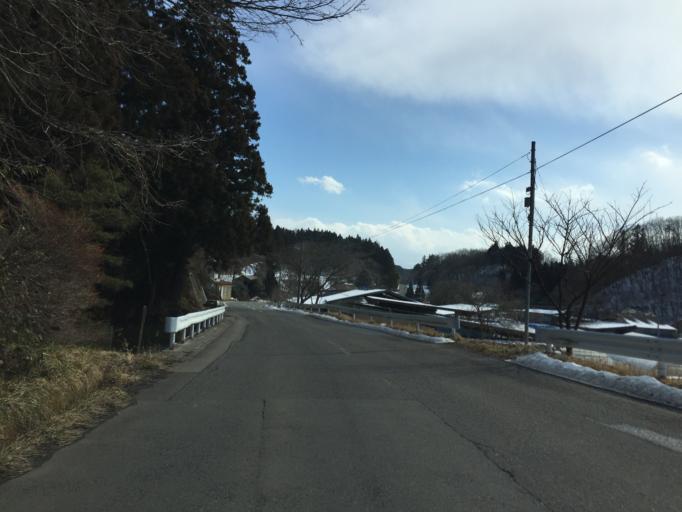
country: JP
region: Fukushima
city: Ishikawa
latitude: 37.1969
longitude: 140.5353
